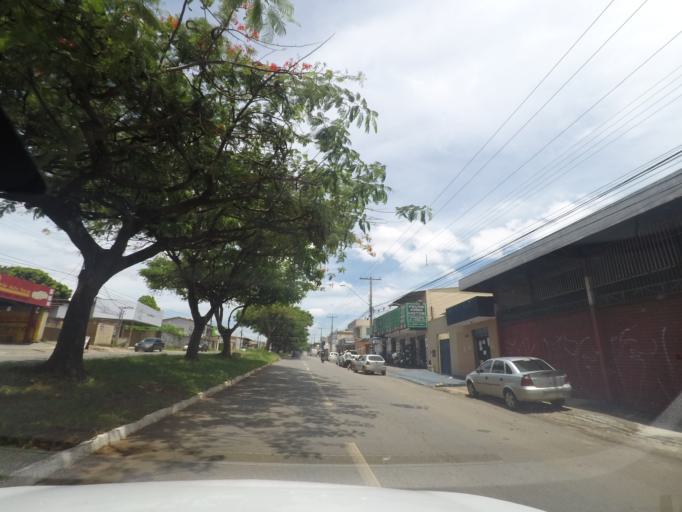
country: BR
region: Goias
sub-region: Goiania
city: Goiania
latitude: -16.6666
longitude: -49.2173
